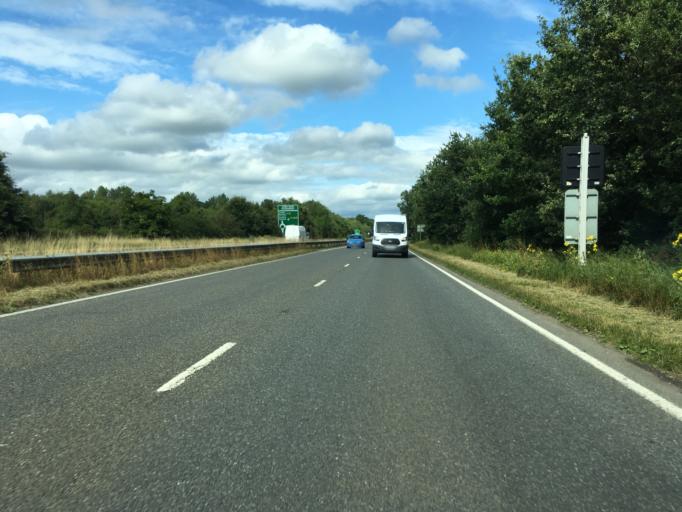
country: GB
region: England
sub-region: West Sussex
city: Horsham
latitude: 51.0764
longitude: -0.3424
